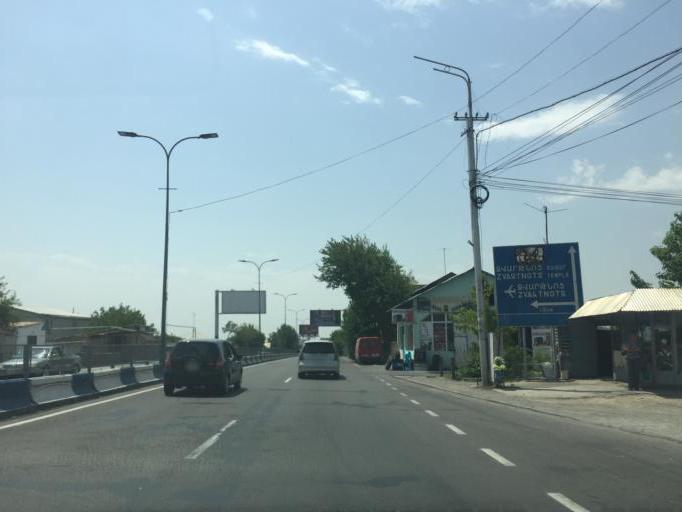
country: AM
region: Armavir
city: Mertsavan
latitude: 40.1646
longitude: 44.4144
